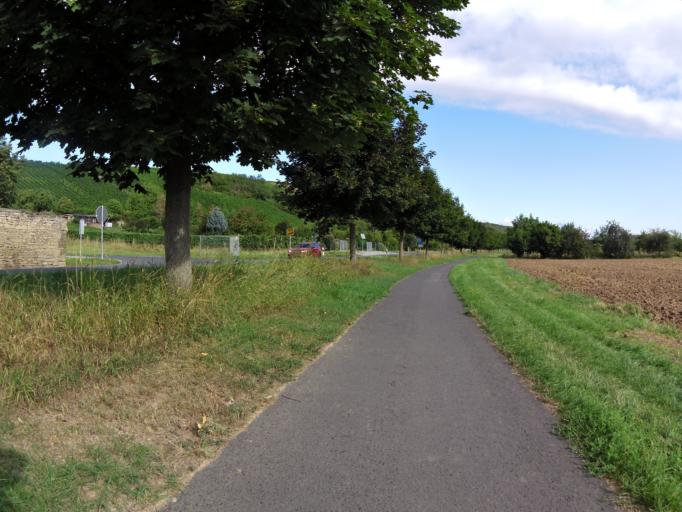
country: DE
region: Bavaria
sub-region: Regierungsbezirk Unterfranken
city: Mainstockheim
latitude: 49.7781
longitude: 10.1519
